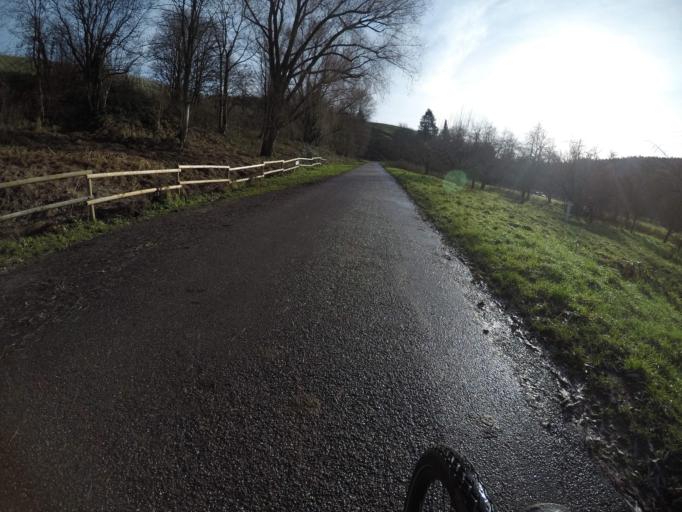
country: DE
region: Baden-Wuerttemberg
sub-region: Regierungsbezirk Stuttgart
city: Weinstadt-Endersbach
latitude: 48.7772
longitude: 9.3390
